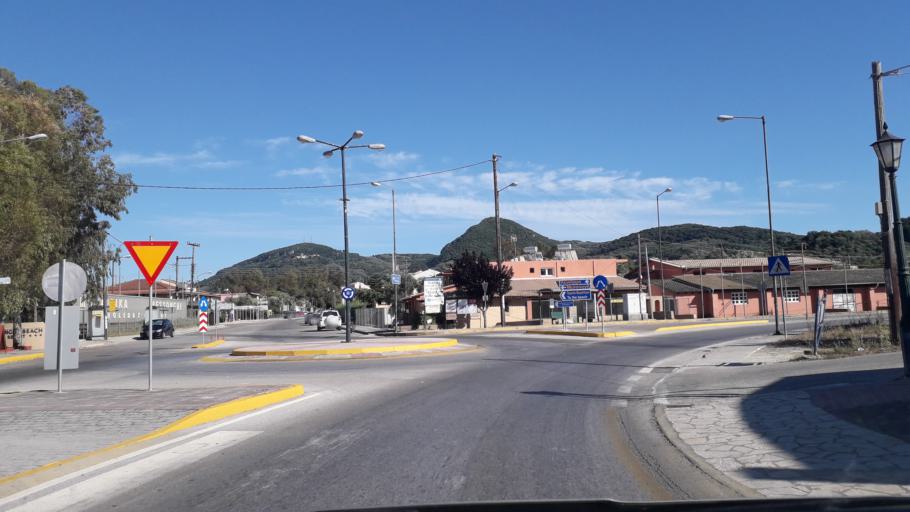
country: GR
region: Ionian Islands
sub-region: Nomos Kerkyras
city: Agios Matthaios
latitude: 39.4792
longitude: 19.9266
